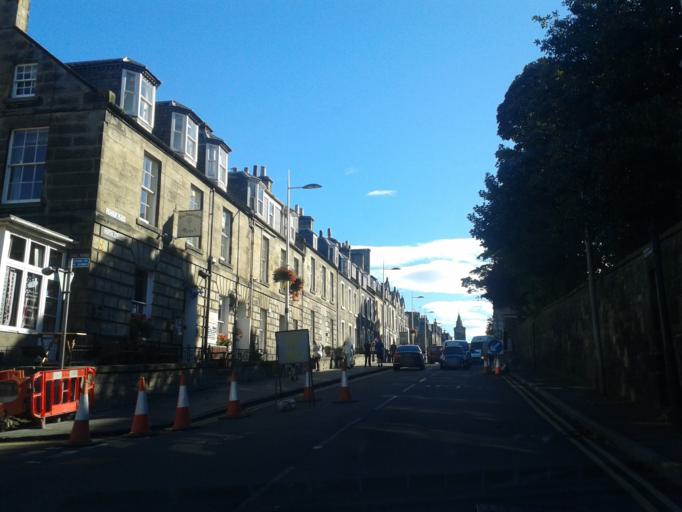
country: GB
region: Scotland
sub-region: Fife
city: Saint Andrews
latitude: 56.3421
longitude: -2.8025
